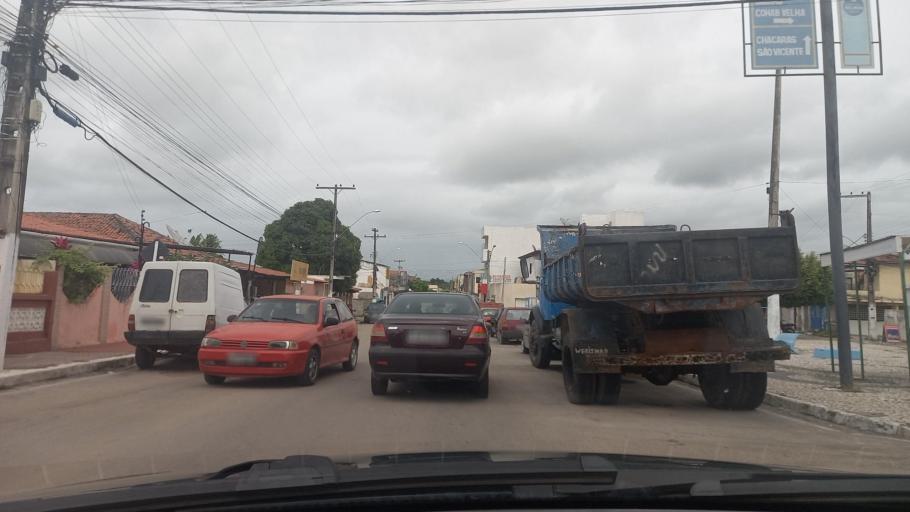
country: BR
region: Alagoas
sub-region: Delmiro Gouveia
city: Delmiro Gouveia
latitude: -9.3869
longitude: -37.9983
